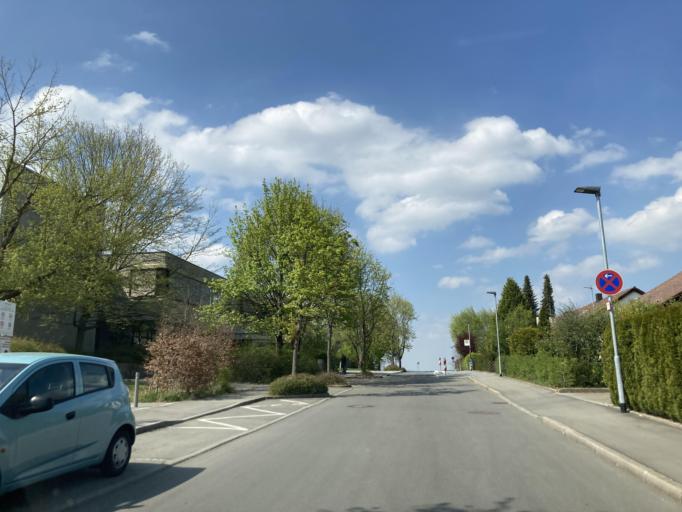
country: DE
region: Baden-Wuerttemberg
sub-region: Tuebingen Region
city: Kusterdingen
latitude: 48.5251
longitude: 9.1155
